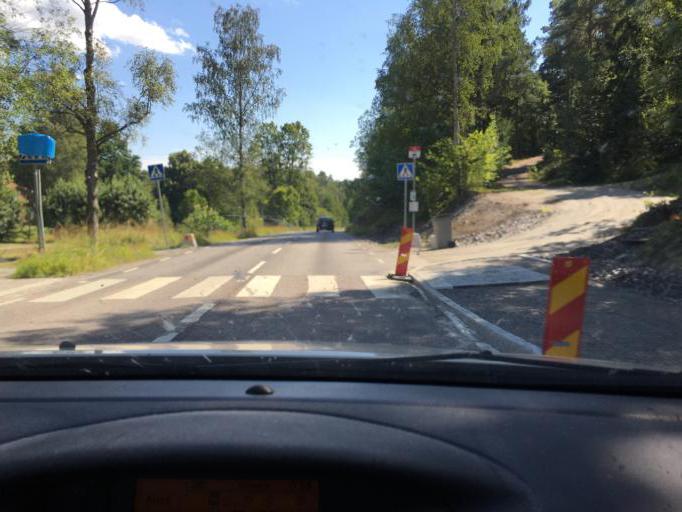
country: SE
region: Stockholm
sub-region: Varmdo Kommun
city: Gustavsberg
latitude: 59.2882
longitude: 18.4088
